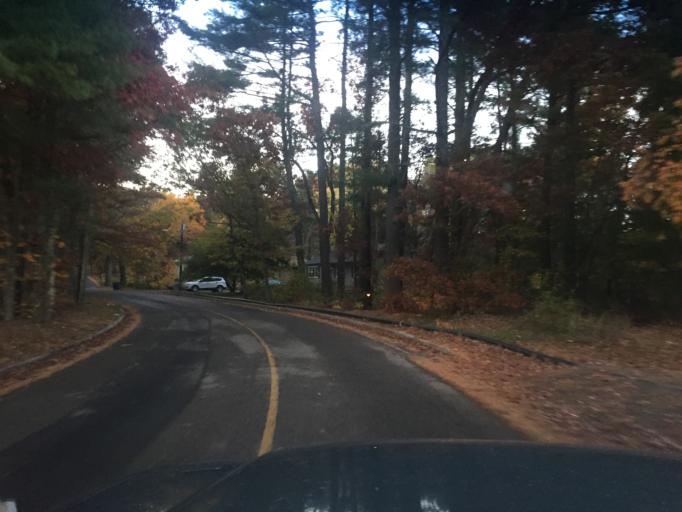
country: US
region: Massachusetts
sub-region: Norfolk County
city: Medway
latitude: 42.1561
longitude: -71.3953
